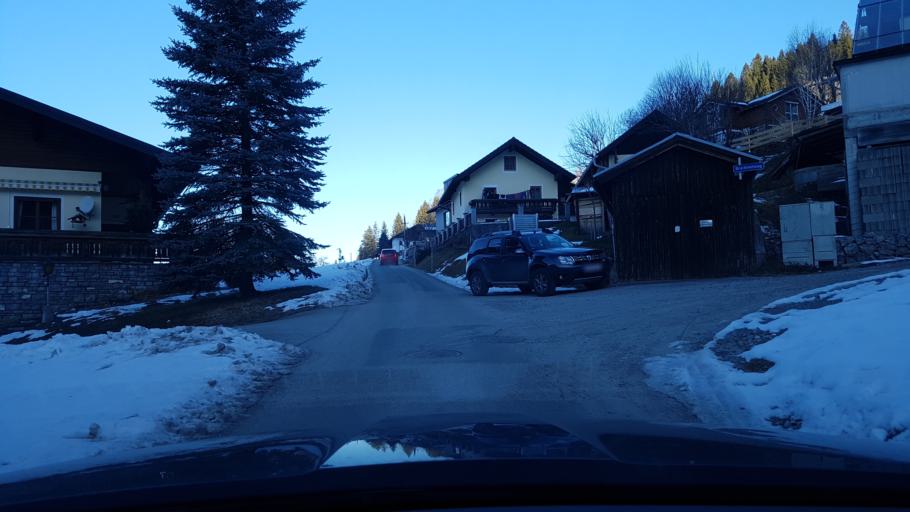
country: AT
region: Salzburg
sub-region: Politischer Bezirk Hallein
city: Scheffau am Tennengebirge
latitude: 47.6454
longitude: 13.2309
